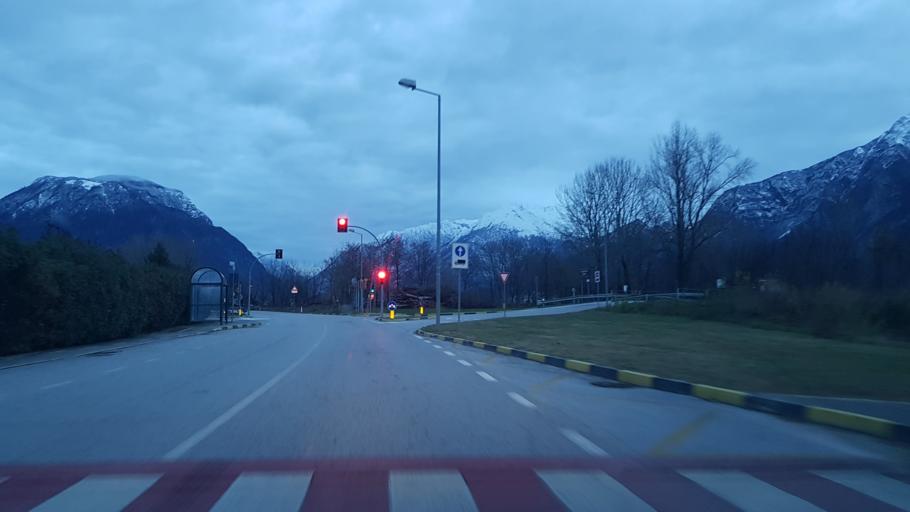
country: IT
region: Friuli Venezia Giulia
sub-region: Provincia di Udine
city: Gemona
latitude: 46.2758
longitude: 13.1000
